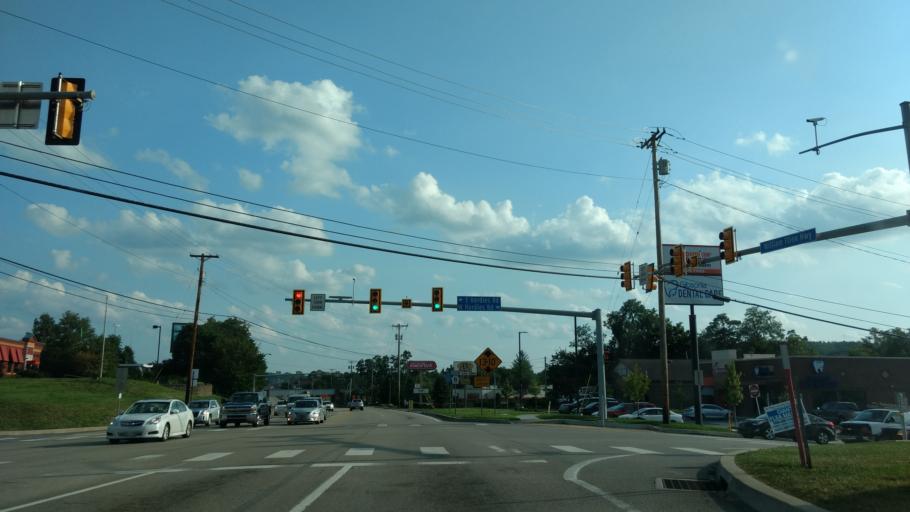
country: US
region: Pennsylvania
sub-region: Allegheny County
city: Gibsonia
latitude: 40.6142
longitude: -79.9474
